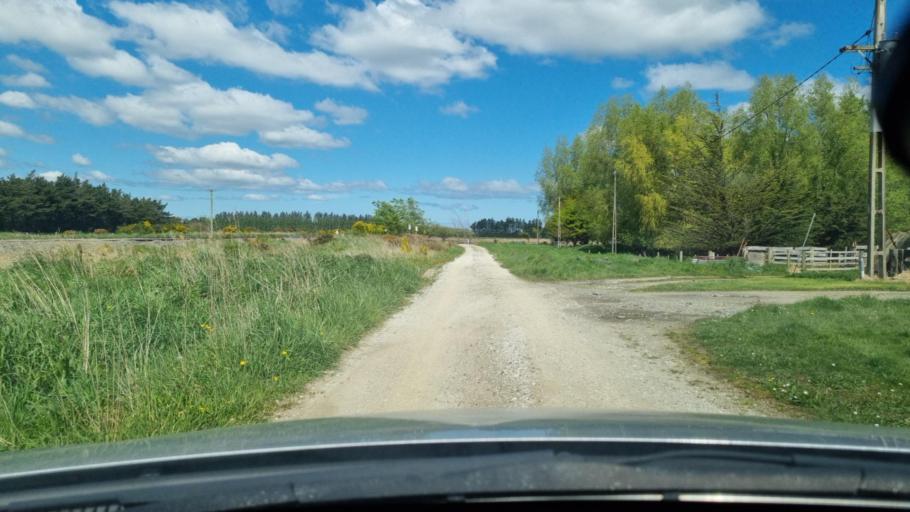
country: NZ
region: Southland
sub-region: Invercargill City
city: Invercargill
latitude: -46.3484
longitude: 168.3400
